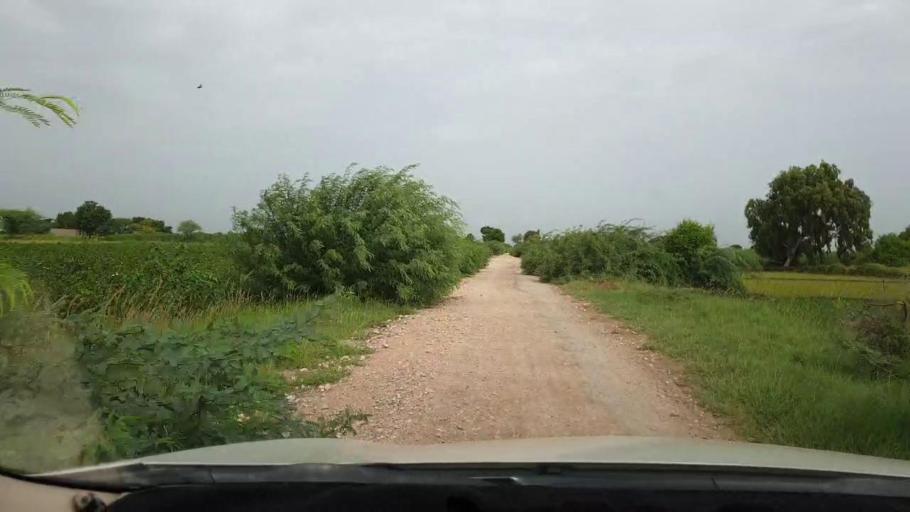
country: PK
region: Sindh
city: Matli
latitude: 25.1066
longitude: 68.6148
